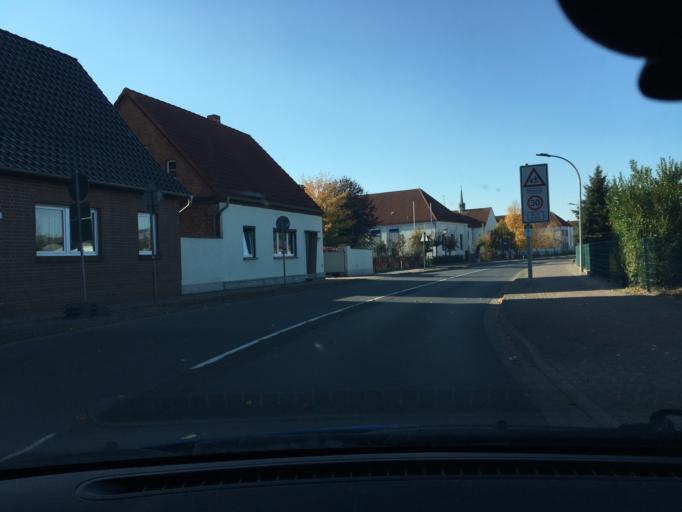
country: DE
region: Mecklenburg-Vorpommern
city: Domitz
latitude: 53.1348
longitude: 11.2703
